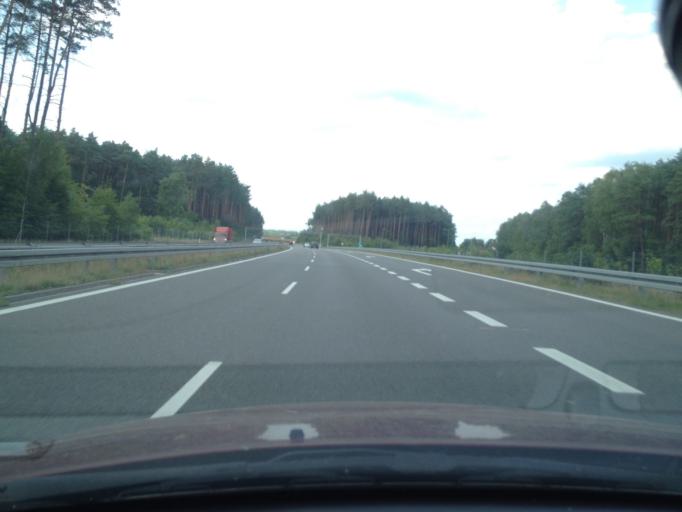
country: PL
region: West Pomeranian Voivodeship
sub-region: Powiat goleniowski
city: Goleniow
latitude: 53.6047
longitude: 14.8232
